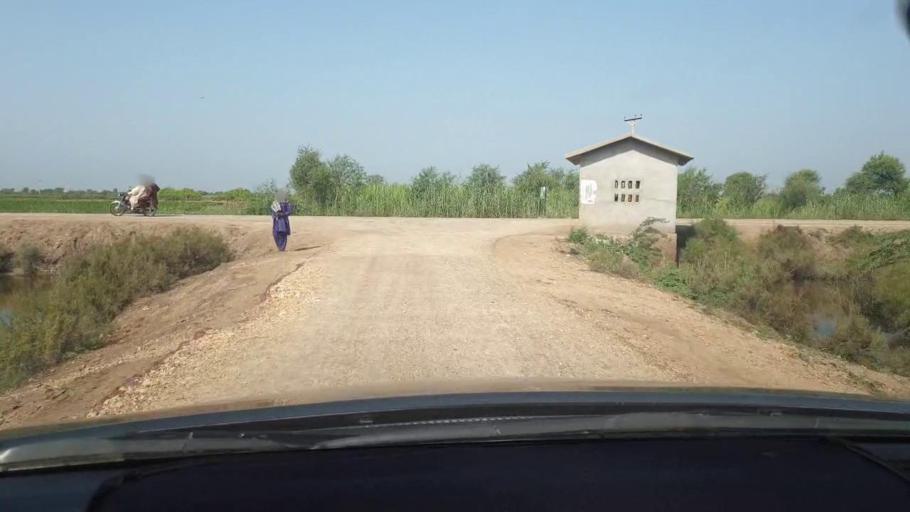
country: PK
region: Sindh
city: Tando Bago
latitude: 24.6800
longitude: 69.1282
